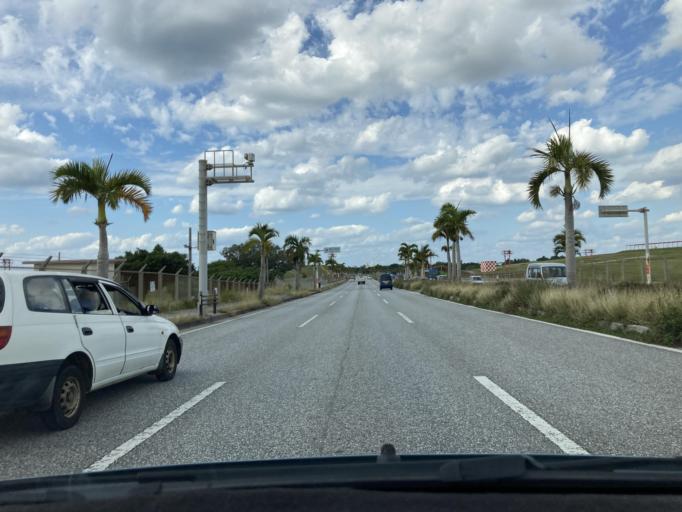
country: JP
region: Okinawa
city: Chatan
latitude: 26.3424
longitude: 127.7491
